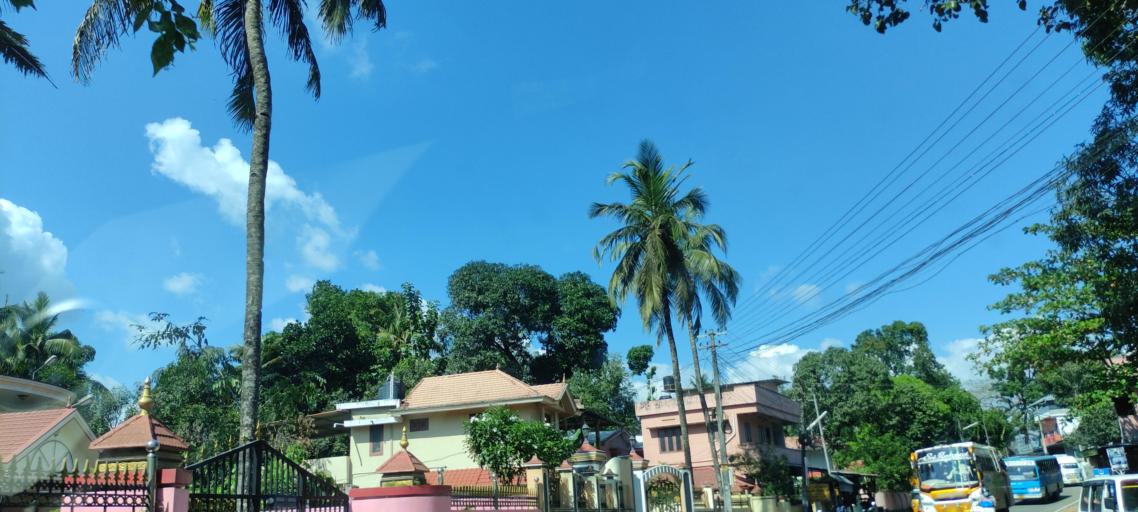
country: IN
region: Kerala
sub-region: Pattanamtitta
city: Adur
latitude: 9.1609
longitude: 76.7436
